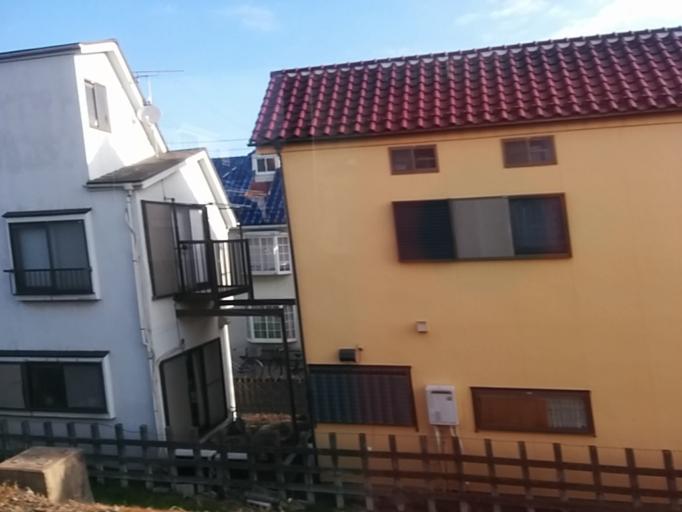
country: JP
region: Saitama
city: Kamifukuoka
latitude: 35.8826
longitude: 139.5045
